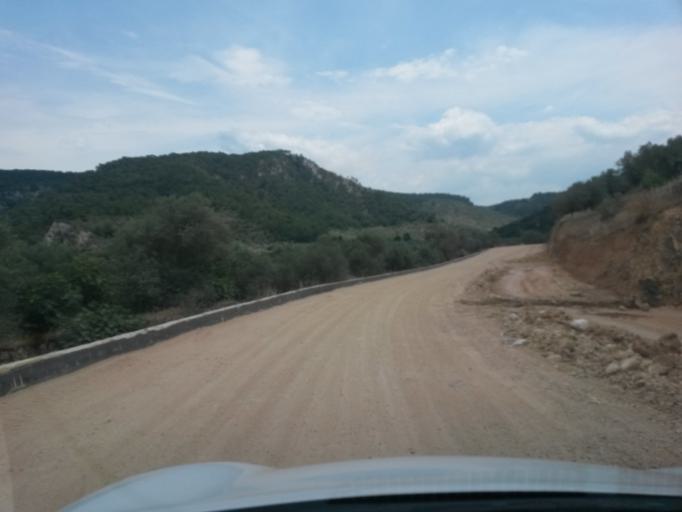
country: GR
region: North Aegean
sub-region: Nomos Lesvou
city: Pamfylla
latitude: 39.1777
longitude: 26.4229
